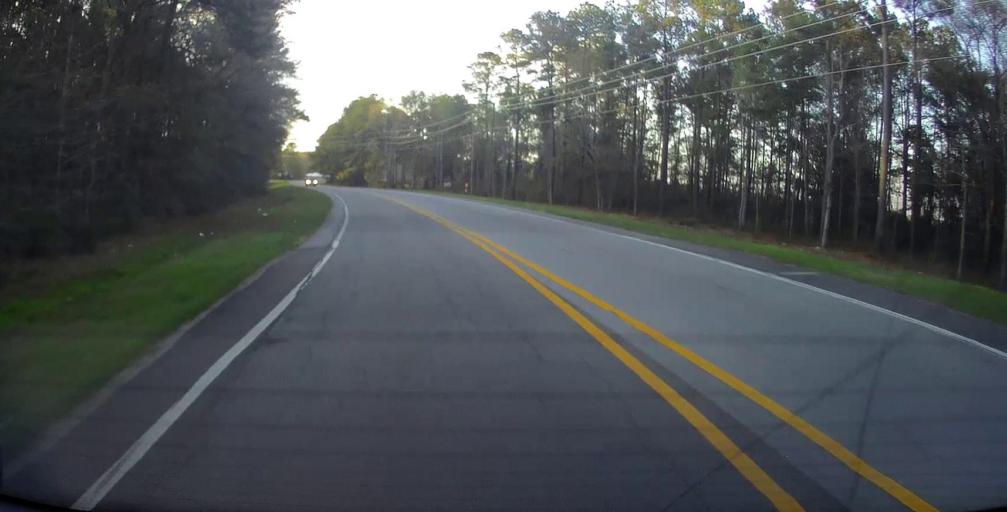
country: US
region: Georgia
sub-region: Chatham County
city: Bloomingdale
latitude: 32.1309
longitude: -81.3862
